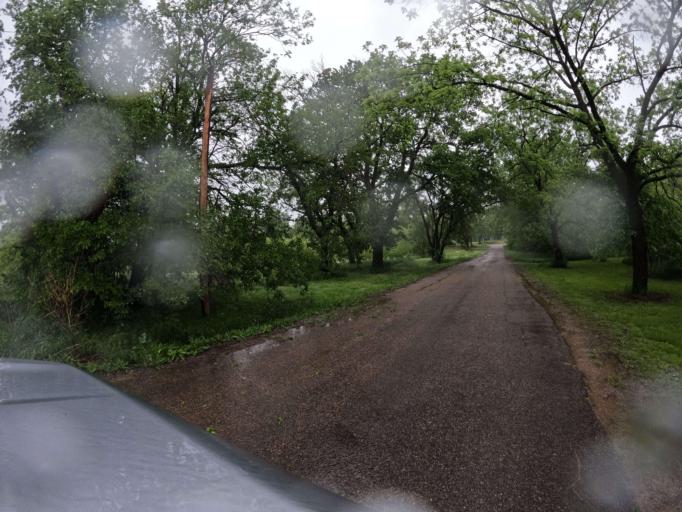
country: US
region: Nebraska
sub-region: Gage County
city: Wymore
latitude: 40.1234
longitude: -96.6544
